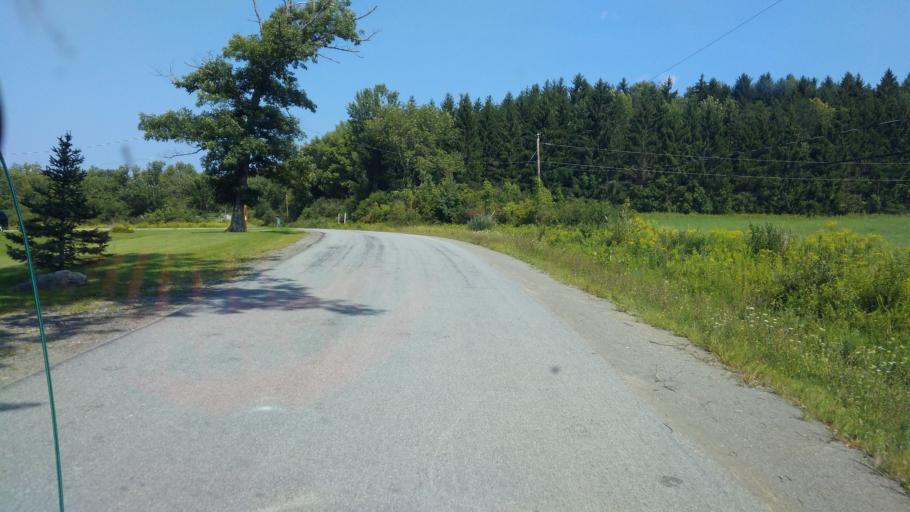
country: US
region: New York
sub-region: Allegany County
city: Belmont
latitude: 42.3142
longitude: -78.0672
